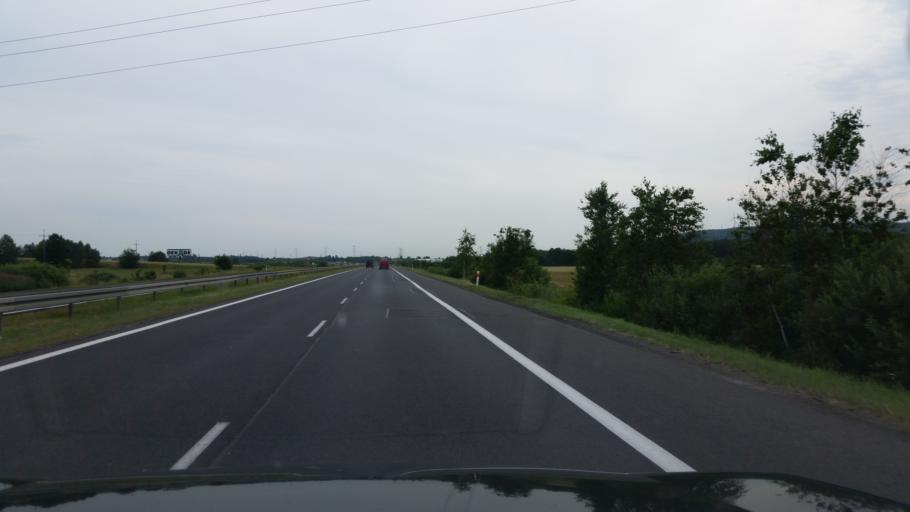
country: PL
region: Lodz Voivodeship
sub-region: Powiat radomszczanski
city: Kamiensk
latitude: 51.2225
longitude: 19.5009
